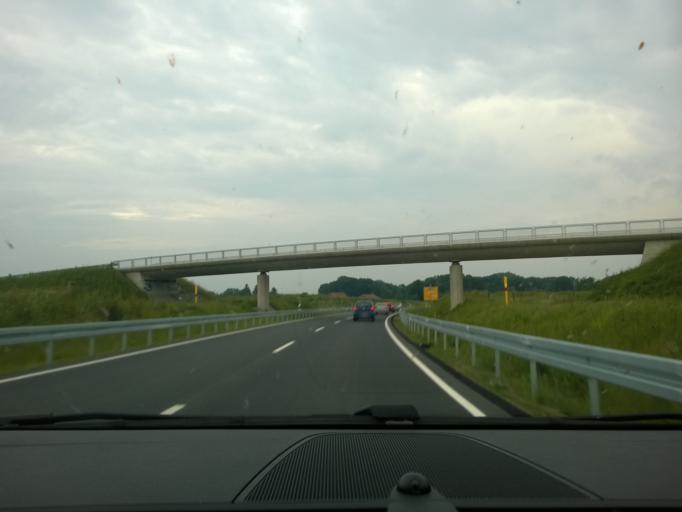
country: DE
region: North Rhine-Westphalia
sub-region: Regierungsbezirk Munster
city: Nottuln
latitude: 51.9352
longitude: 7.3683
